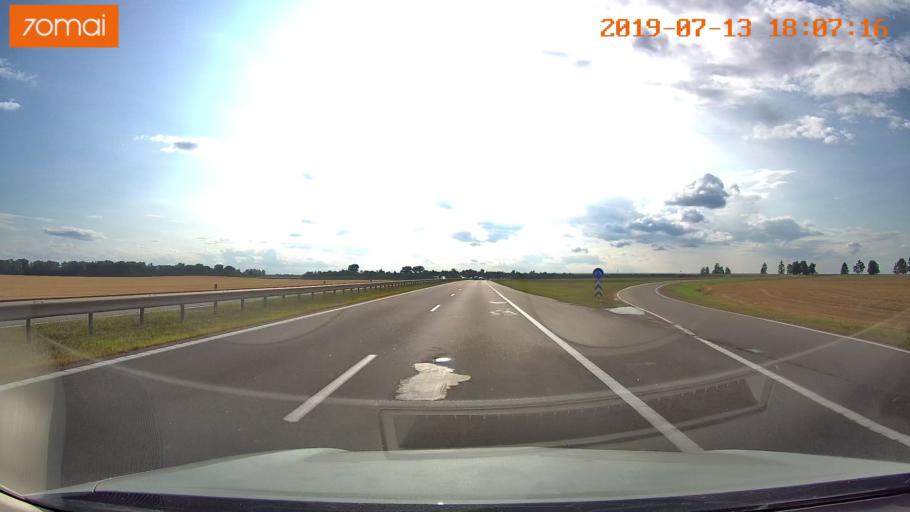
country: BY
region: Minsk
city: Blon'
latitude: 53.5453
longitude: 28.1815
